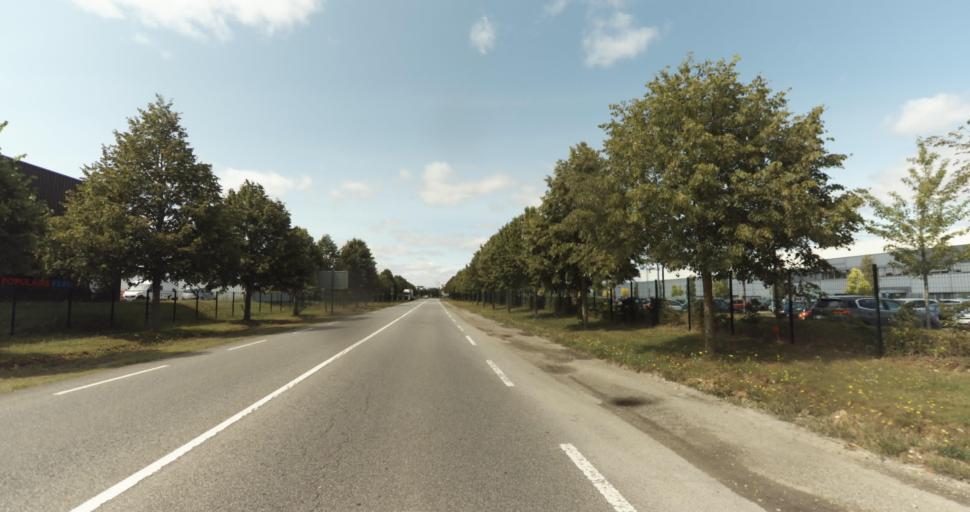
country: FR
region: Haute-Normandie
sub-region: Departement de l'Eure
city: Evreux
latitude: 49.0041
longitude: 1.1760
